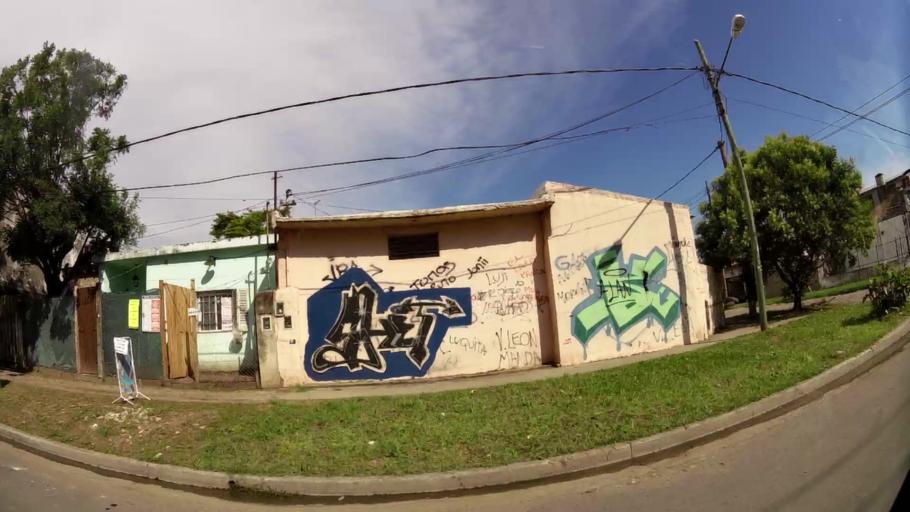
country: AR
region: Buenos Aires
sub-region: Partido de Merlo
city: Merlo
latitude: -34.6310
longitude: -58.7114
